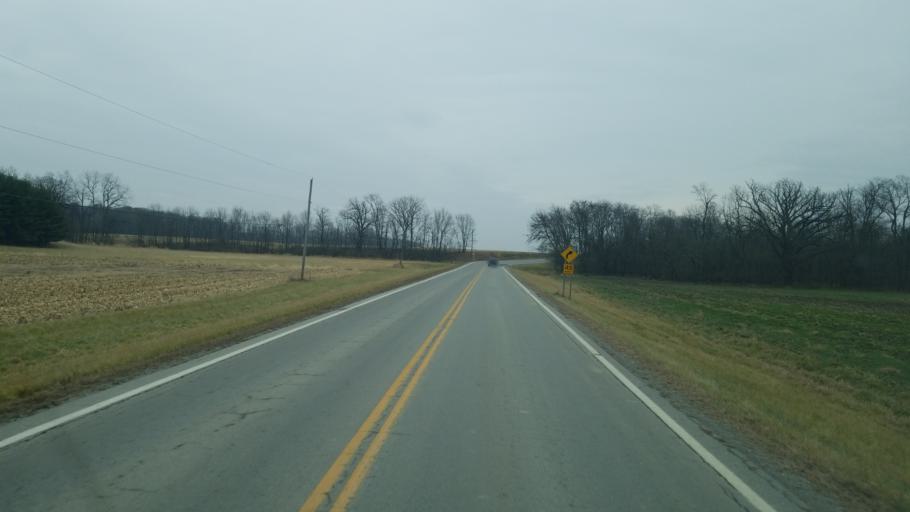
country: US
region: Ohio
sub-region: Hardin County
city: Forest
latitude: 40.7074
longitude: -83.4358
